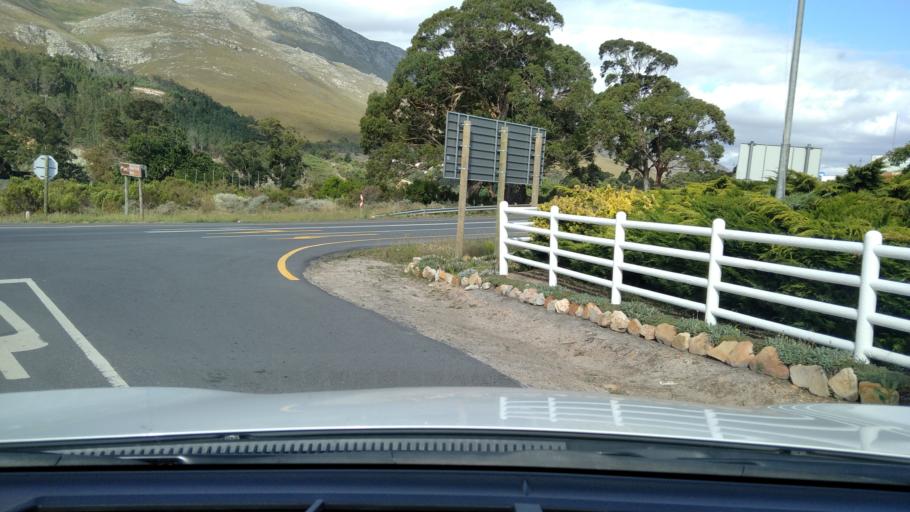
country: ZA
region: Western Cape
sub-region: Overberg District Municipality
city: Grabouw
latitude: -34.2069
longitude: 19.1492
